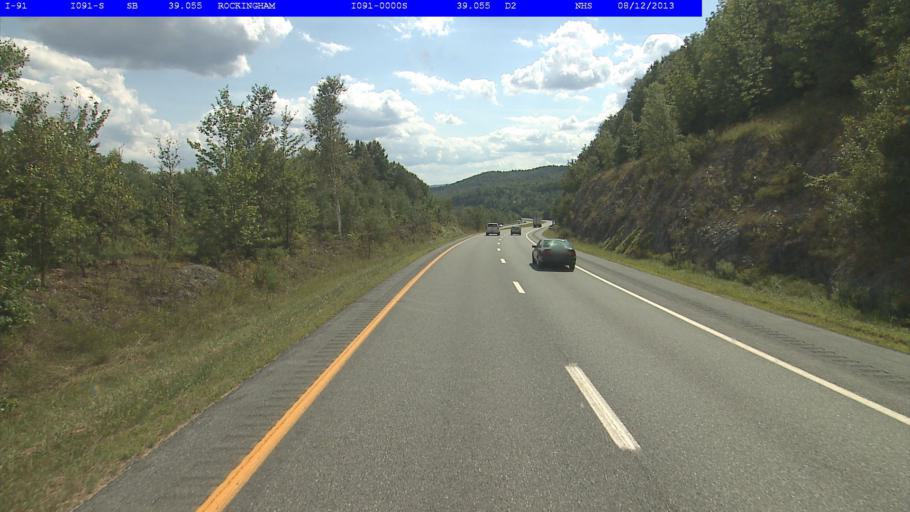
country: US
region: New Hampshire
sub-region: Sullivan County
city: Charlestown
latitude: 43.2323
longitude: -72.4486
